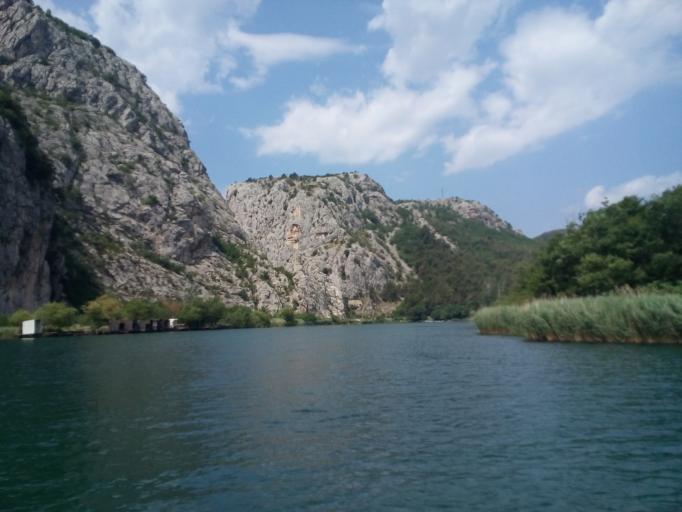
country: HR
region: Splitsko-Dalmatinska
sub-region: Grad Omis
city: Omis
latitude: 43.4511
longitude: 16.7018
